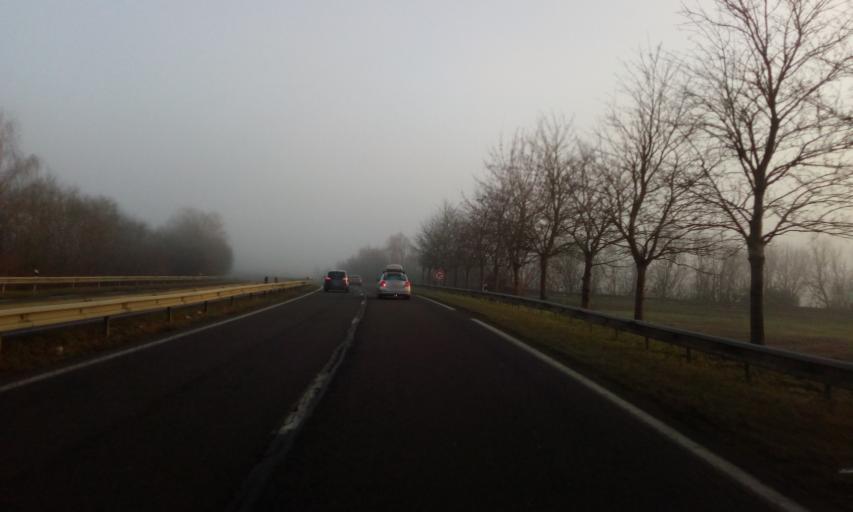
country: FR
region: Champagne-Ardenne
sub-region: Departement des Ardennes
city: Tournes
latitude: 49.7930
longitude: 4.6339
